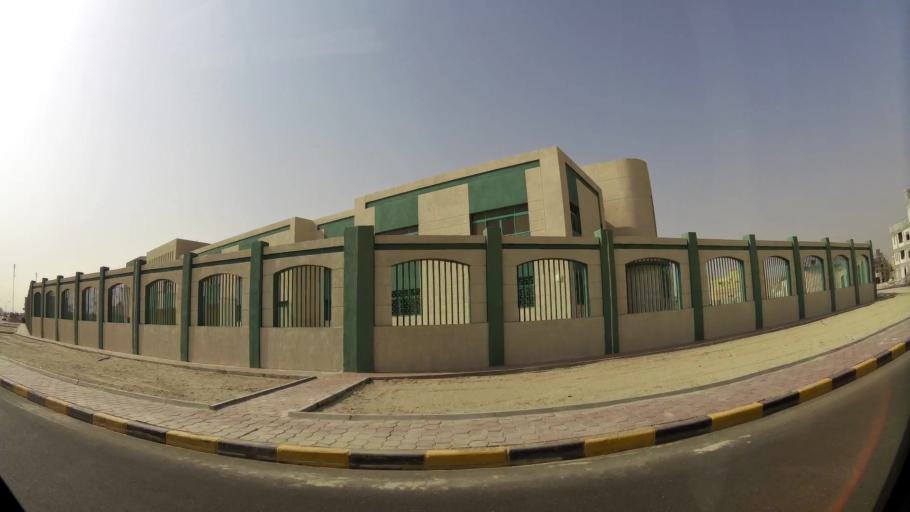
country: KW
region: Muhafazat al Jahra'
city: Al Jahra'
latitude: 29.3588
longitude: 47.7620
